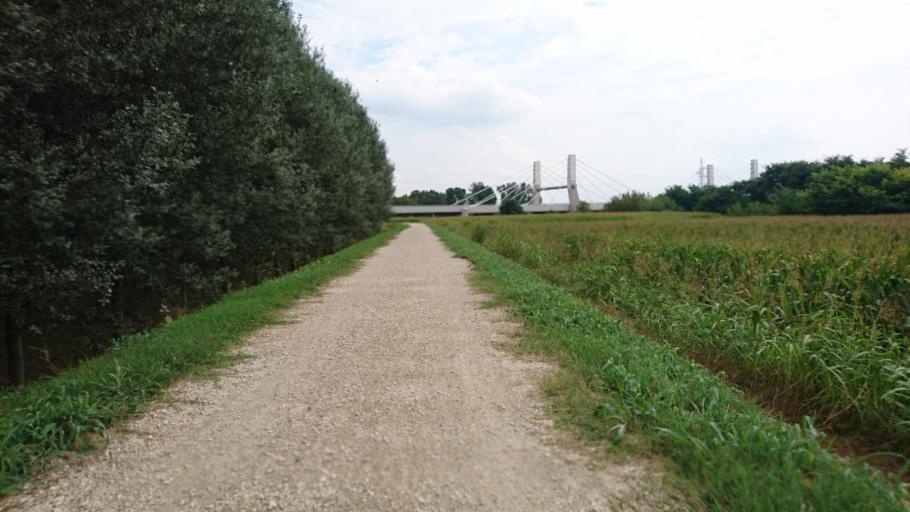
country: IT
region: Veneto
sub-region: Provincia di Vicenza
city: Longare
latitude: 45.4652
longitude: 11.6304
